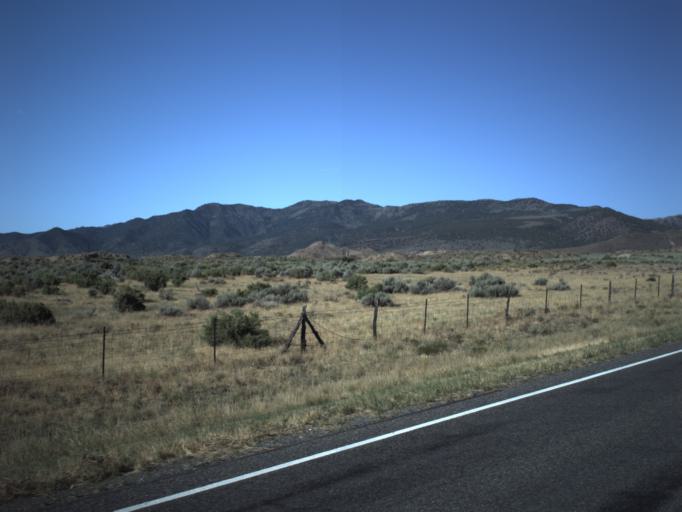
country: US
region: Utah
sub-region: Utah County
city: Genola
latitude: 39.9517
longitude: -111.9810
